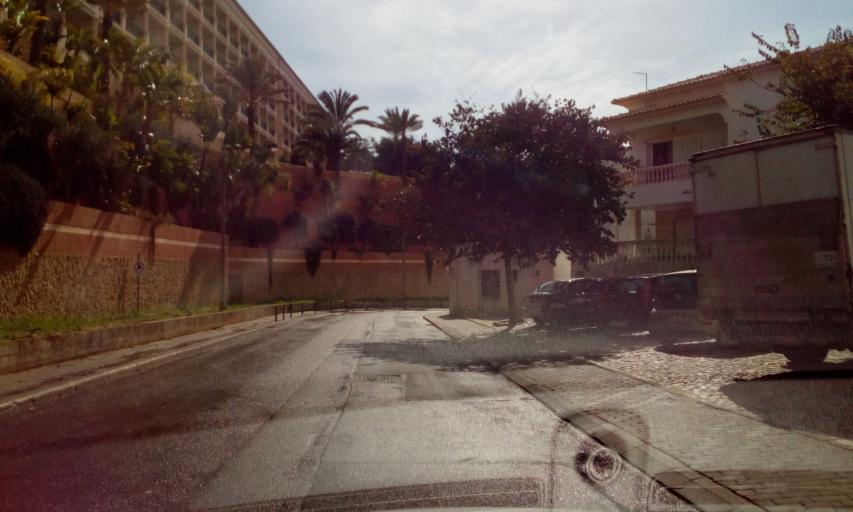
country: PT
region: Faro
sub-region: Loule
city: Boliqueime
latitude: 37.0922
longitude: -8.1883
